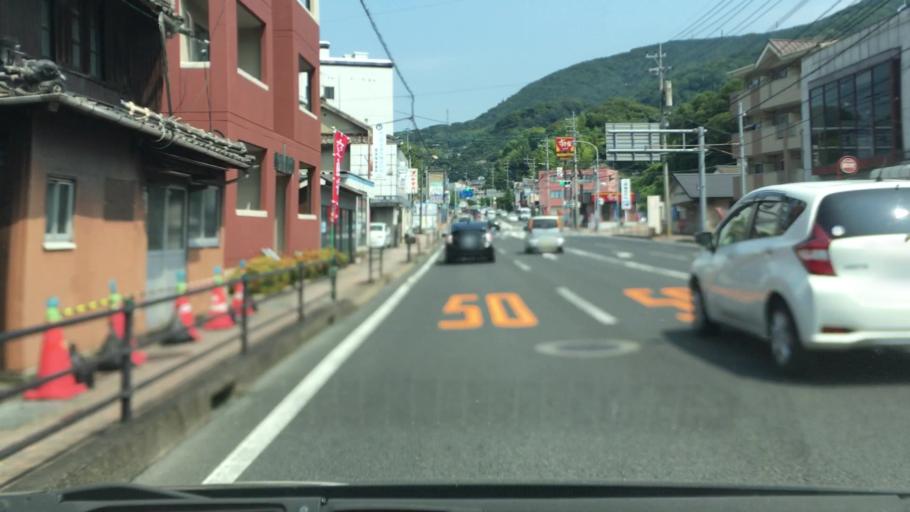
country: JP
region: Nagasaki
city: Sasebo
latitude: 33.1579
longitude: 129.7518
